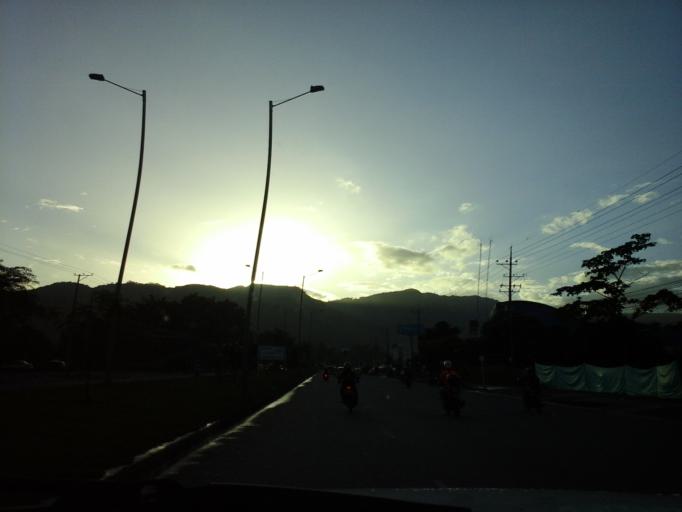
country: CO
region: Meta
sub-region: Villavicencio
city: Villavicencio
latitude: 4.1171
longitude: -73.6365
